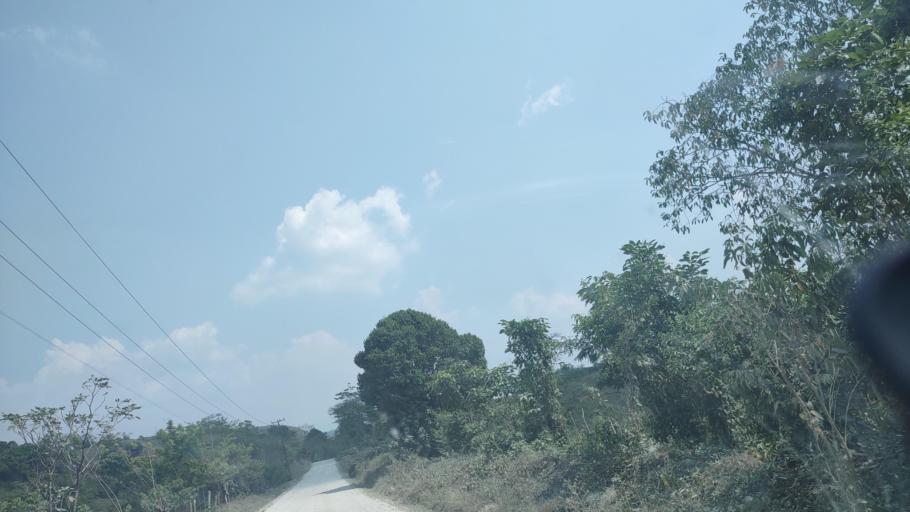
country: MX
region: Tabasco
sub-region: Huimanguillo
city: Francisco Rueda
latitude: 17.5908
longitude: -93.8937
